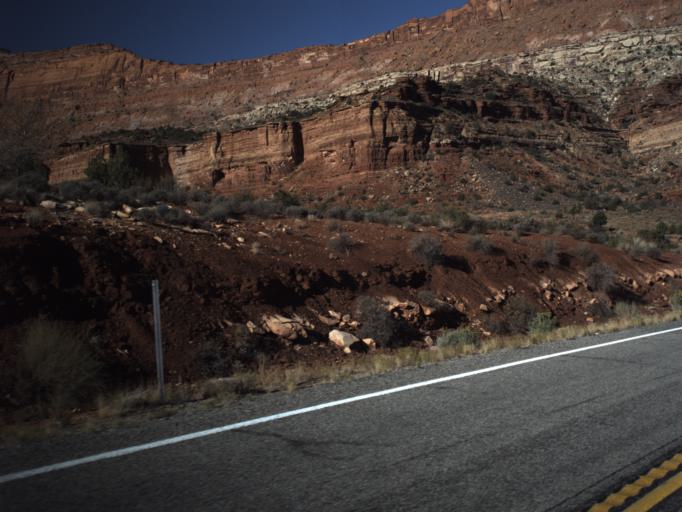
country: US
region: Utah
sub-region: San Juan County
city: Blanding
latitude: 37.7418
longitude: -110.2790
